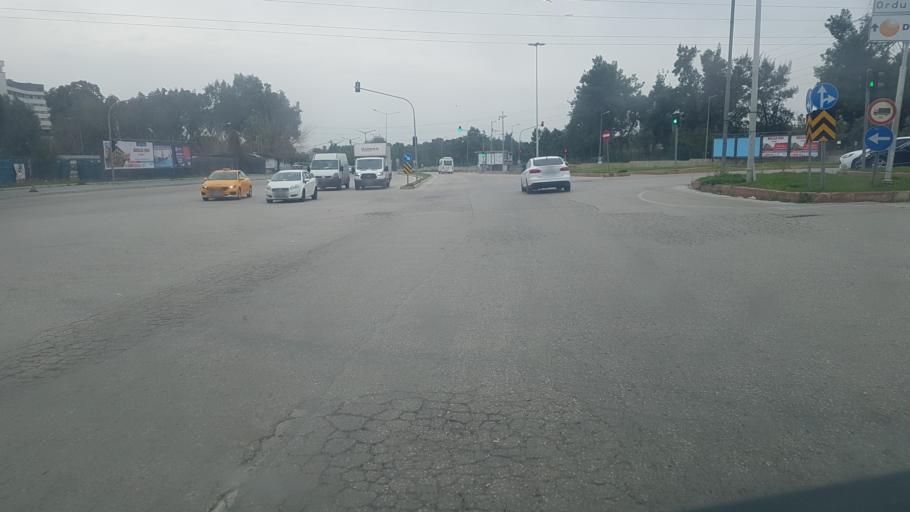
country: TR
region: Adana
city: Adana
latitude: 37.0334
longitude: 35.3469
